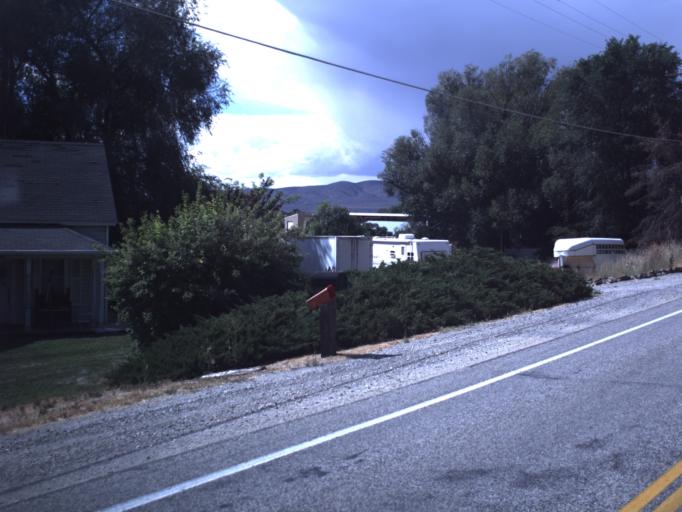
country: US
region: Utah
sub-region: Box Elder County
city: Elwood
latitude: 41.7115
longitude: -112.0909
